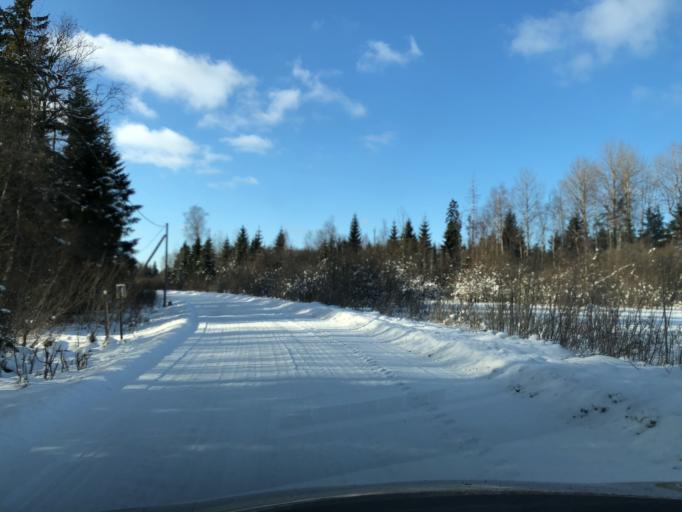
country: EE
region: Jaervamaa
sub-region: Paide linn
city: Paide
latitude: 59.0604
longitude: 25.4928
